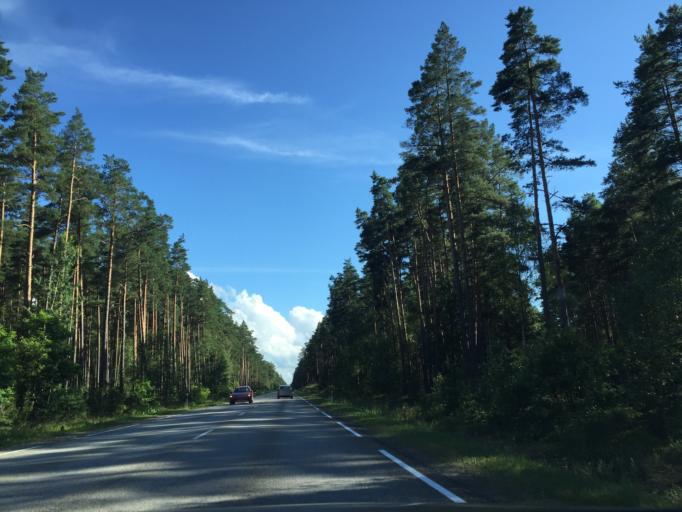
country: LV
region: Riga
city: Jaunciems
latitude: 57.0692
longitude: 24.1577
